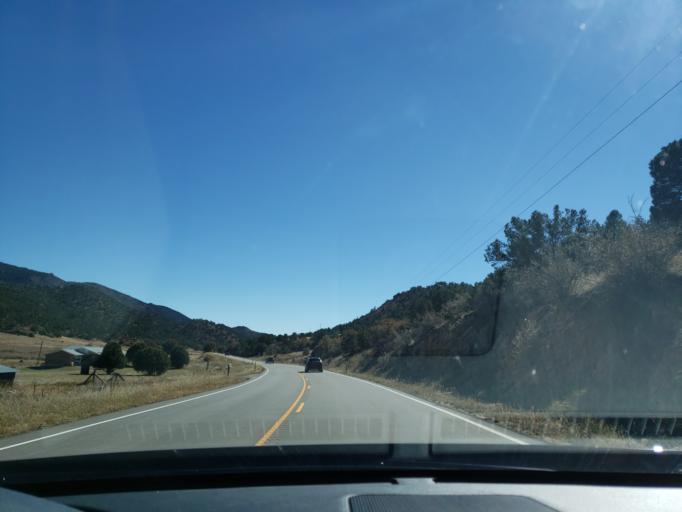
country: US
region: Colorado
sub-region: Fremont County
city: Canon City
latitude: 38.6049
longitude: -105.4356
